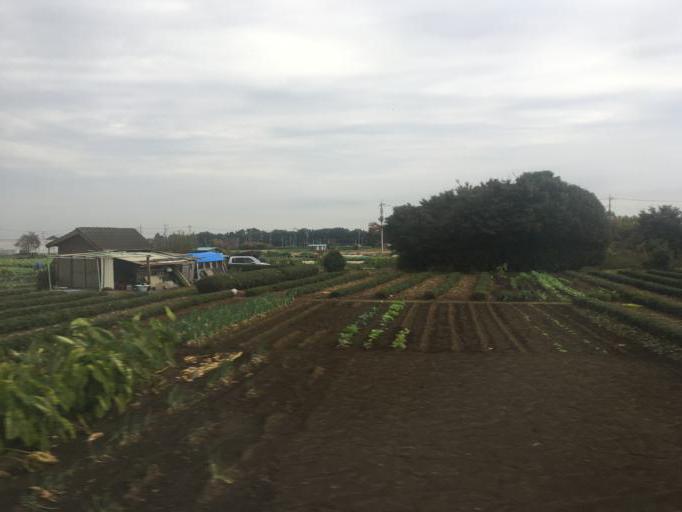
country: JP
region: Saitama
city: Hanno
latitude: 35.8011
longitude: 139.3335
